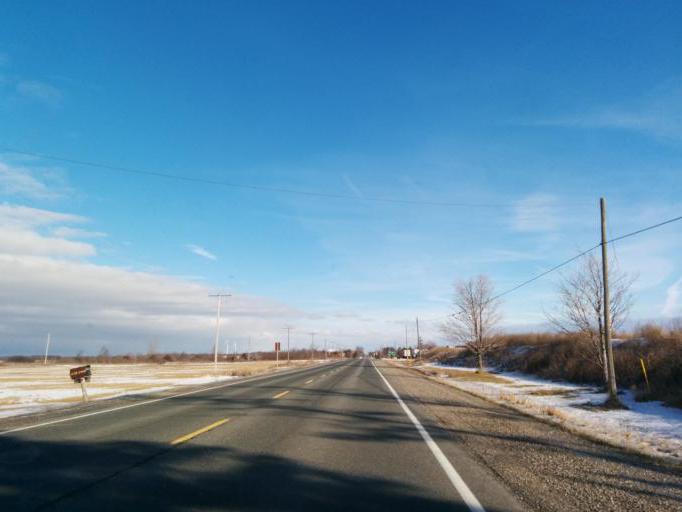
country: CA
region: Ontario
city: Ancaster
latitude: 42.9295
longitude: -79.9431
